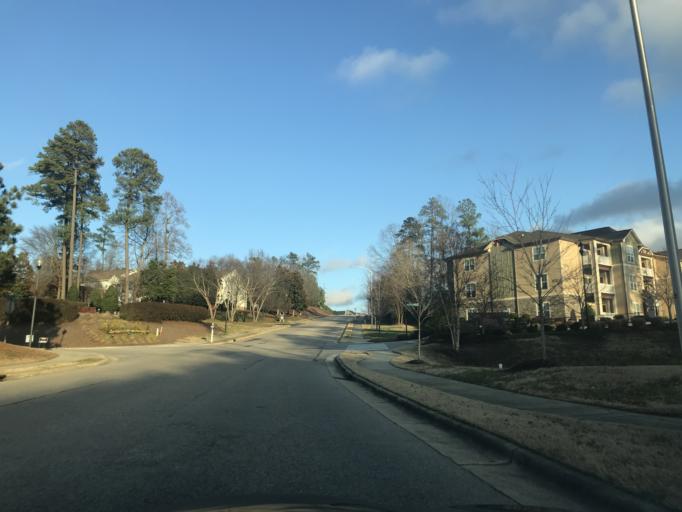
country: US
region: North Carolina
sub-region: Wake County
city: Wake Forest
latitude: 35.9588
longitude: -78.5376
